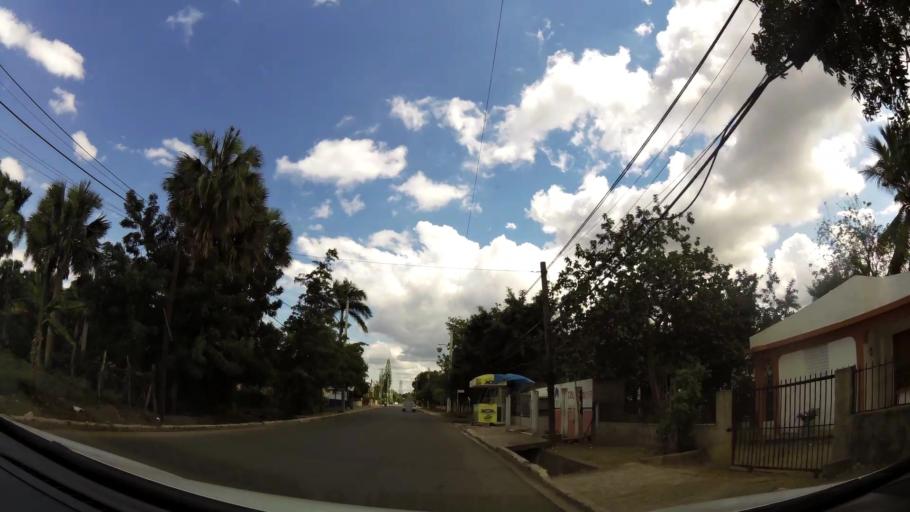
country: DO
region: Santiago
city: Licey al Medio
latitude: 19.3911
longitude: -70.6400
